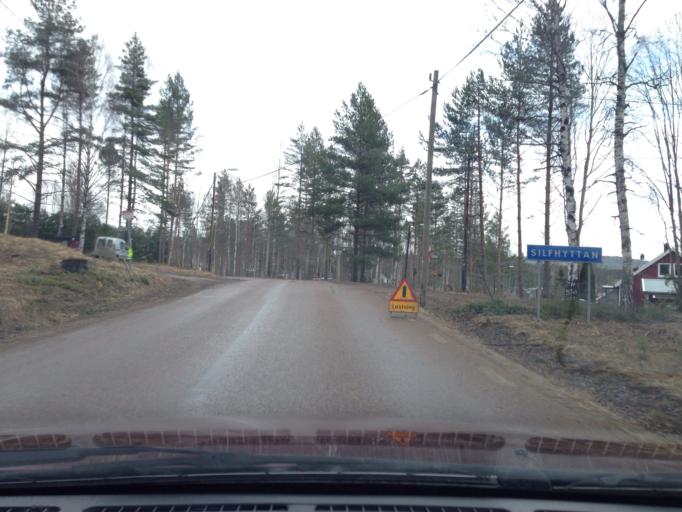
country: SE
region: Dalarna
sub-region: Ludvika Kommun
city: Ludvika
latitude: 60.1750
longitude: 15.2846
